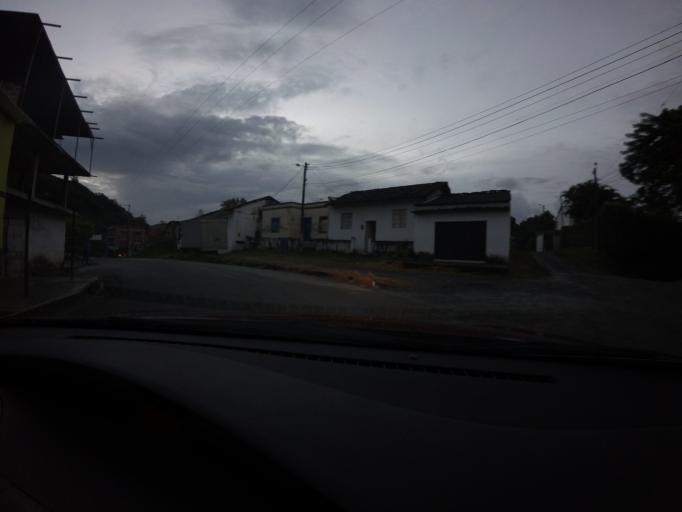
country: CO
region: Caldas
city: Filadelfia
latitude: 5.2980
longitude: -75.5654
